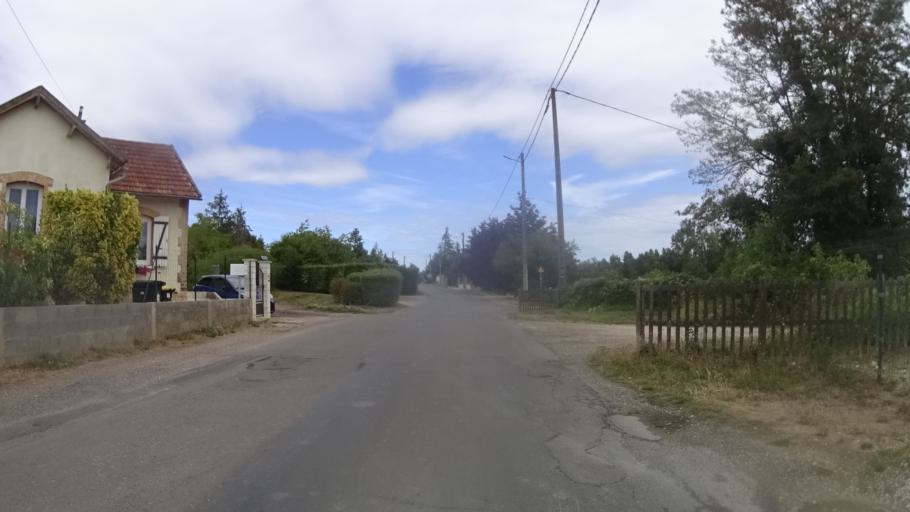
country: FR
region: Centre
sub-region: Departement du Loiret
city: Malesherbes
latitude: 48.2298
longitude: 2.4279
